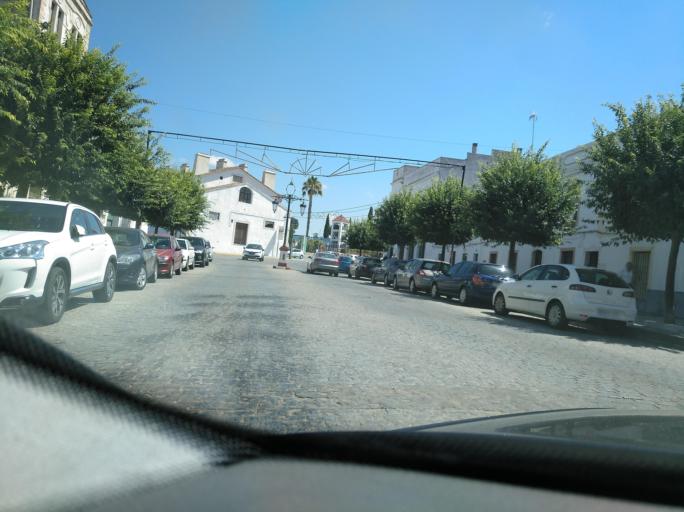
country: ES
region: Extremadura
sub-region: Provincia de Badajoz
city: Olivenza
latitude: 38.6841
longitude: -7.0985
